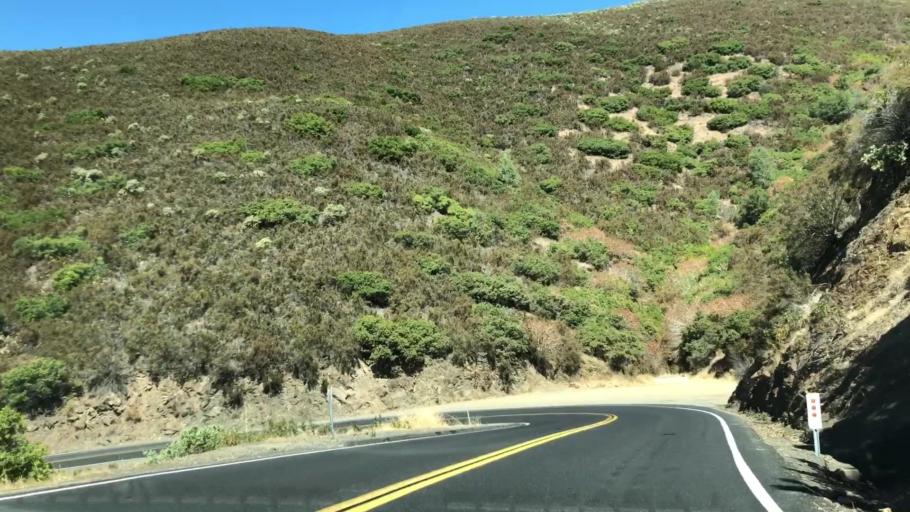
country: US
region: California
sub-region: Tuolumne County
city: Tuolumne City
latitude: 37.8243
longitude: -120.2786
